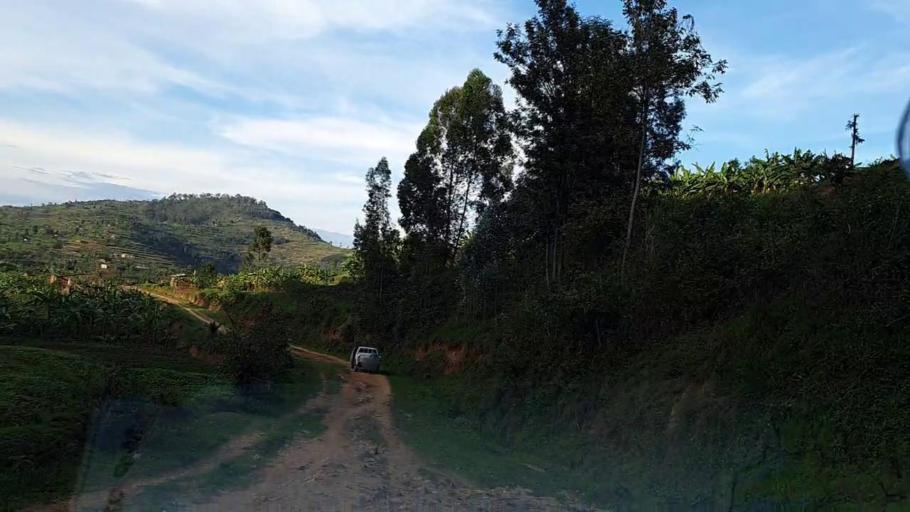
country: RW
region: Southern Province
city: Gikongoro
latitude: -2.4045
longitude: 29.5552
